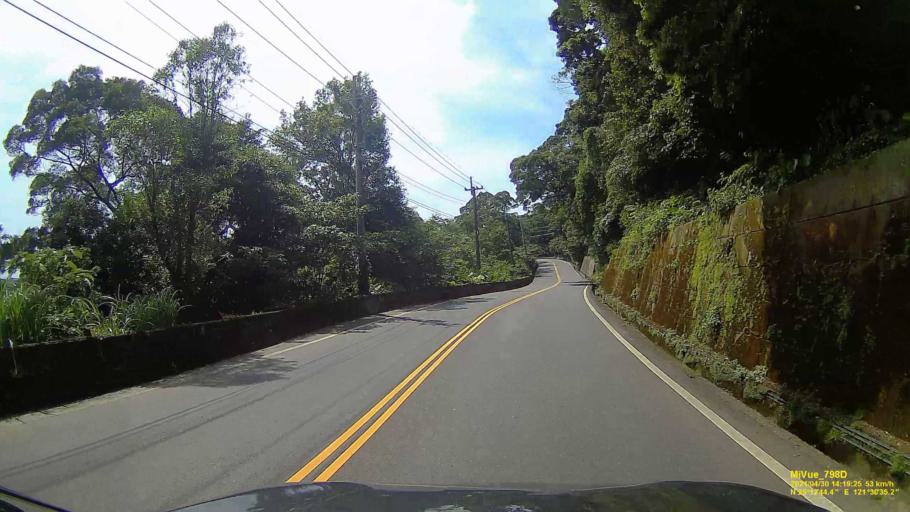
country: TW
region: Taipei
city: Taipei
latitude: 25.2125
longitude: 121.5096
